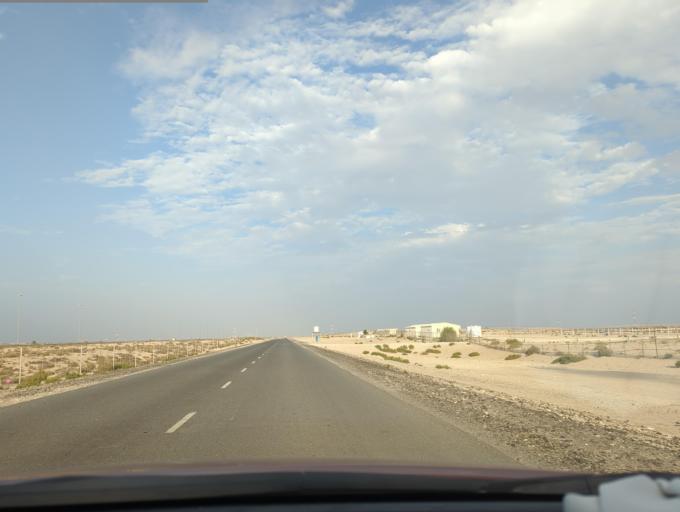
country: AE
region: Dubai
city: Dubai
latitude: 24.7225
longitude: 54.8687
